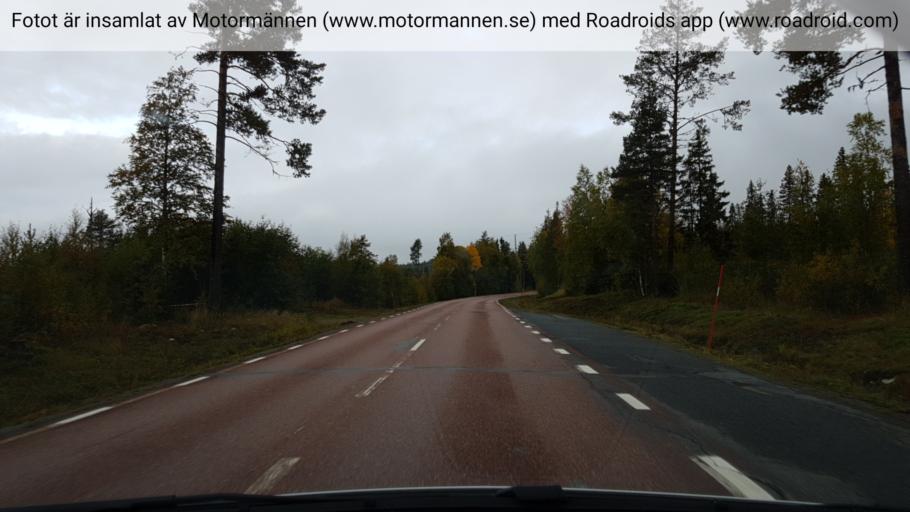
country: SE
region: Vaesterbotten
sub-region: Dorotea Kommun
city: Dorotea
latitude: 64.0668
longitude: 16.0648
